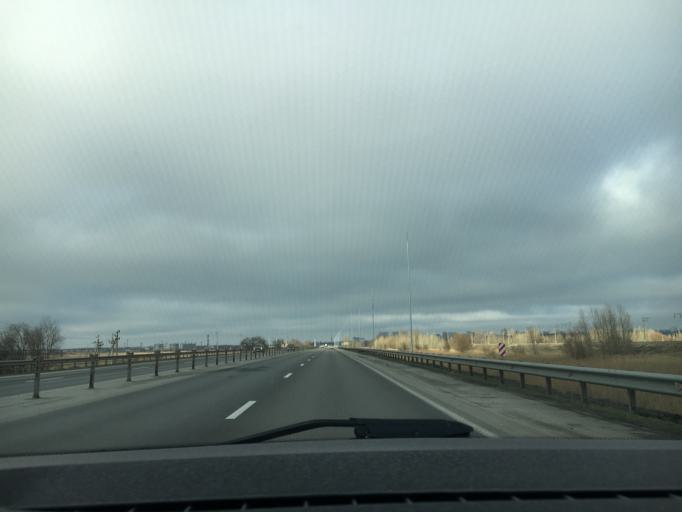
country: RU
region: Rostov
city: Bataysk
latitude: 47.1564
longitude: 39.6596
